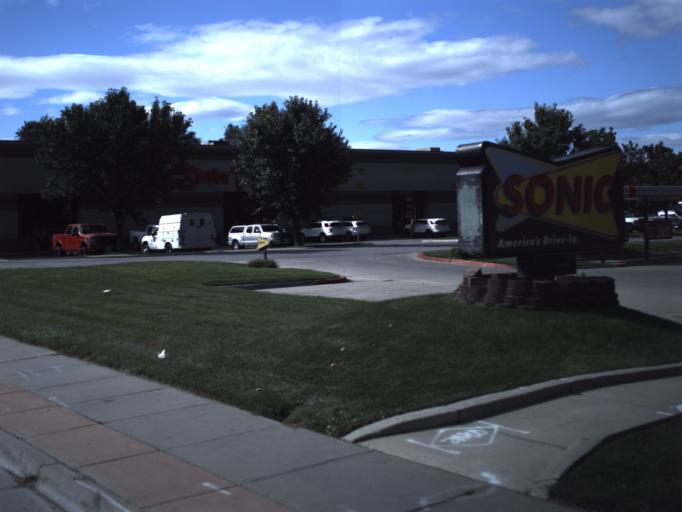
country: US
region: Utah
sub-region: Salt Lake County
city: Taylorsville
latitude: 40.6947
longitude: -111.9390
